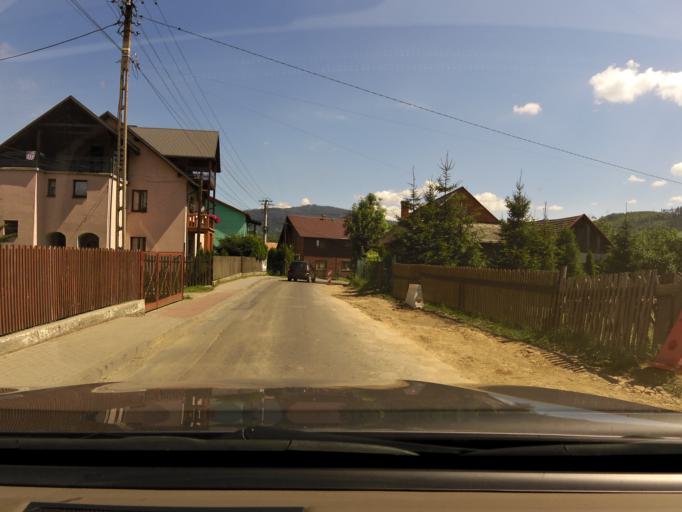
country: PL
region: Silesian Voivodeship
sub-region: Powiat zywiecki
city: Rajcza
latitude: 49.4989
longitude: 19.0890
